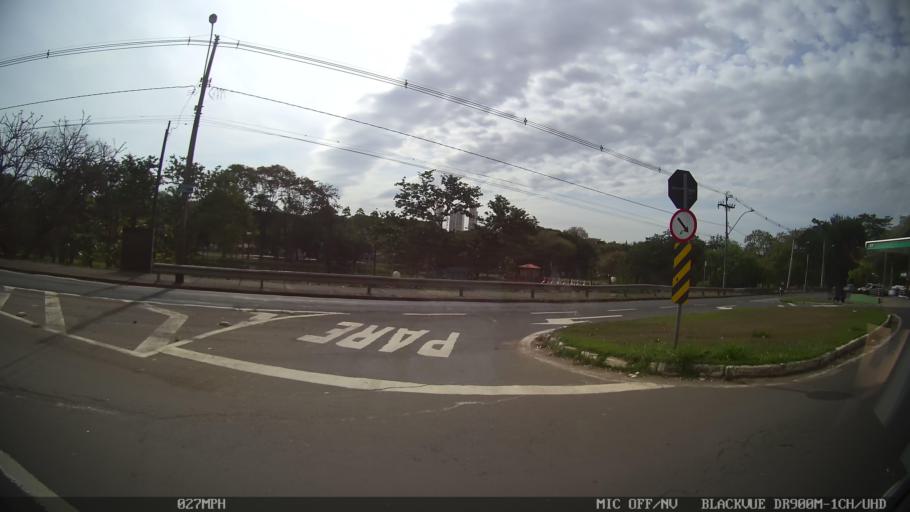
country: BR
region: Sao Paulo
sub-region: Piracicaba
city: Piracicaba
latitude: -22.7277
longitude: -47.6615
